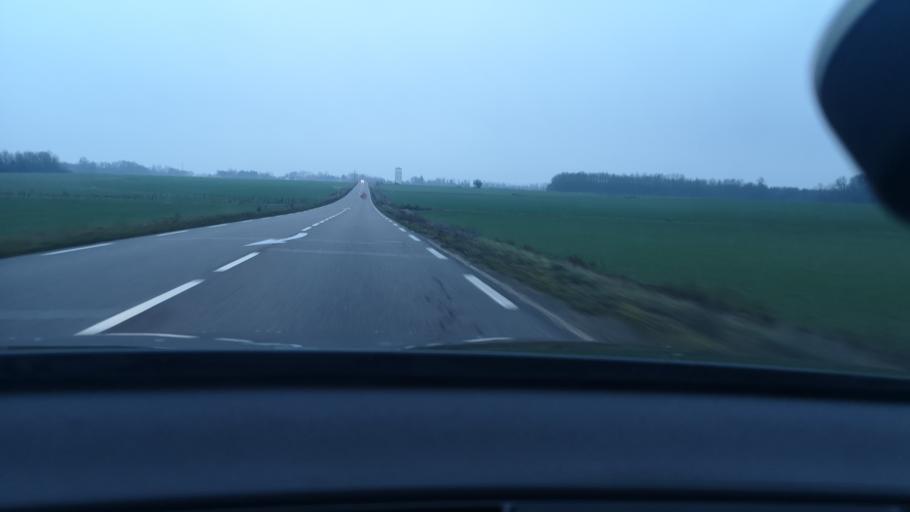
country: FR
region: Bourgogne
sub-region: Departement de la Cote-d'Or
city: Seurre
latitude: 47.0781
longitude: 5.1031
